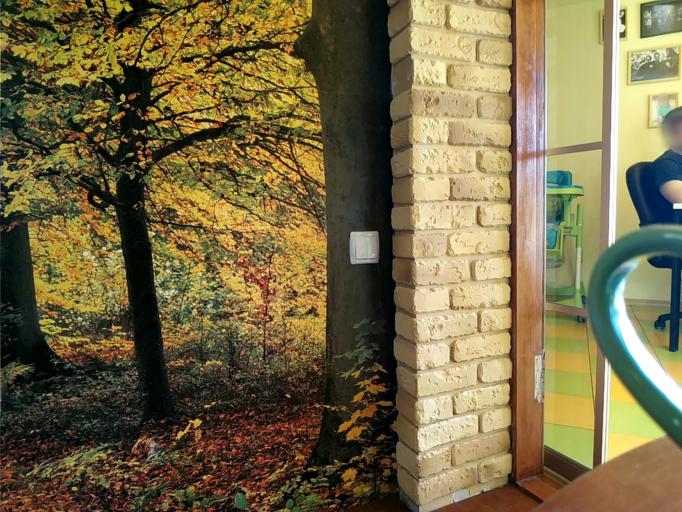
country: RU
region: Moskovskaya
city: Chernogolovka
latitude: 56.0747
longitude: 38.3184
